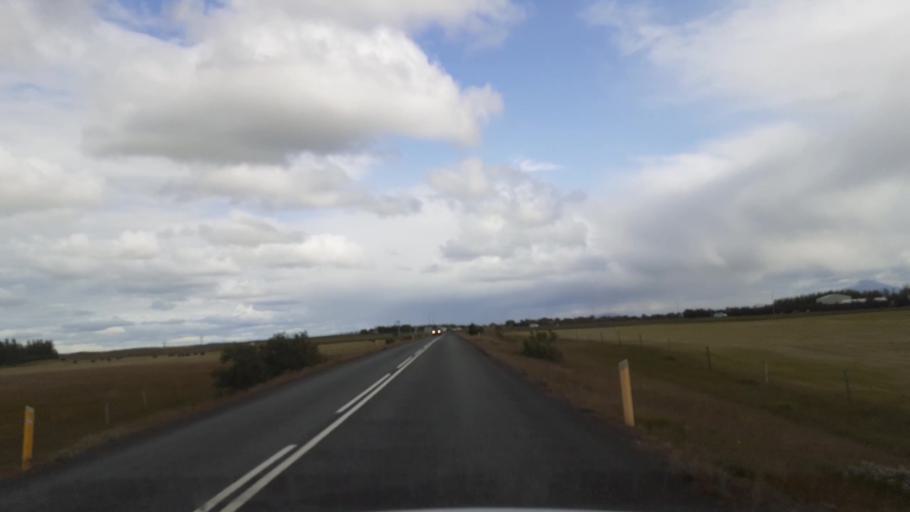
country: IS
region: South
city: Vestmannaeyjar
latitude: 63.8388
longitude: -20.4122
